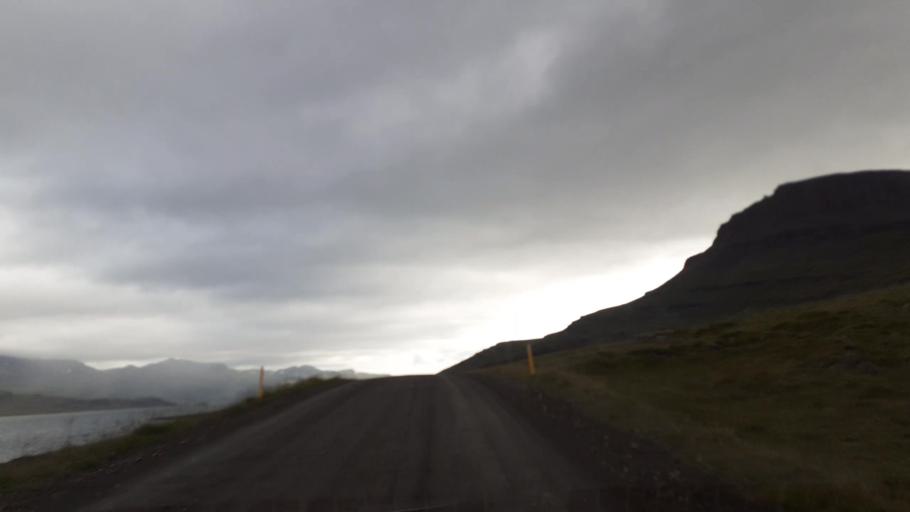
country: IS
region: East
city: Reydarfjoerdur
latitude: 65.0130
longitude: -14.1584
